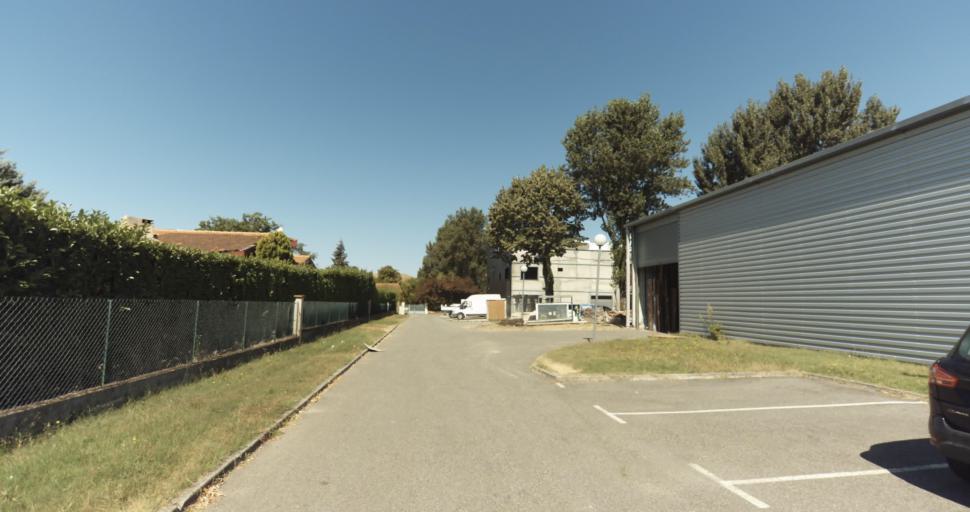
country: FR
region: Midi-Pyrenees
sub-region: Departement de la Haute-Garonne
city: L'Union
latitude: 43.6369
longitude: 1.4937
